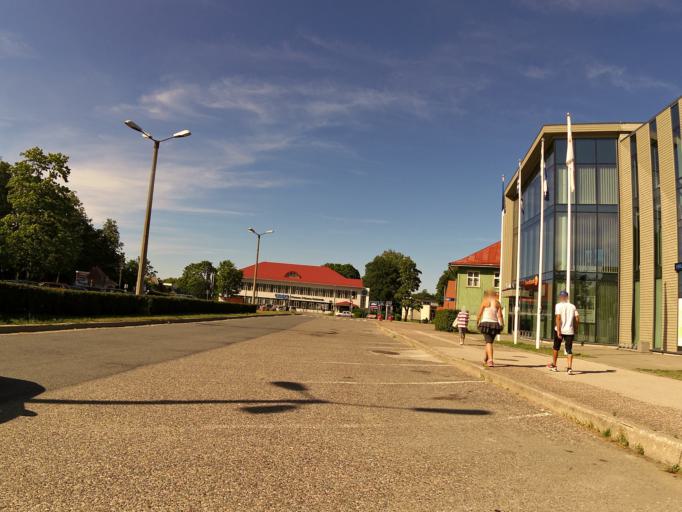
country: EE
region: Hiiumaa
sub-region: Kaerdla linn
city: Kardla
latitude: 58.9973
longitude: 22.7471
